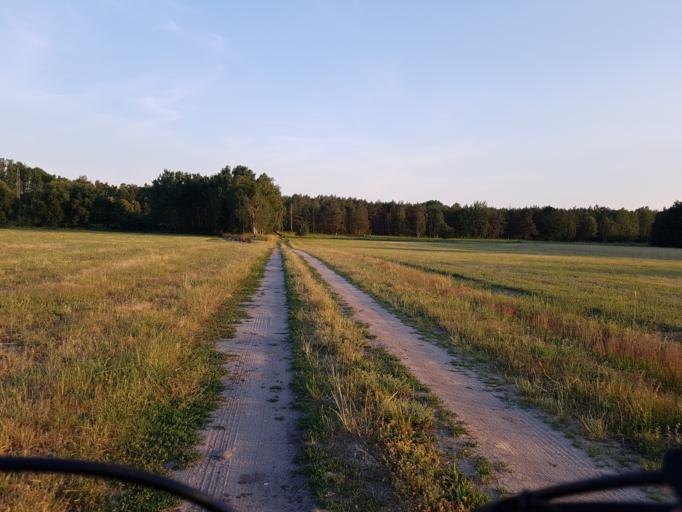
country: DE
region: Brandenburg
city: Trobitz
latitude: 51.5997
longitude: 13.4184
